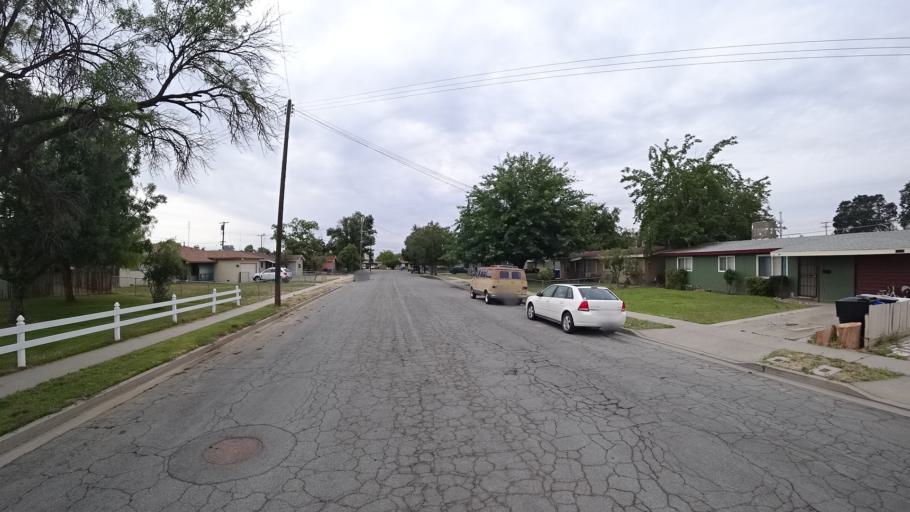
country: US
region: California
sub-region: Kings County
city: Hanford
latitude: 36.3420
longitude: -119.6606
